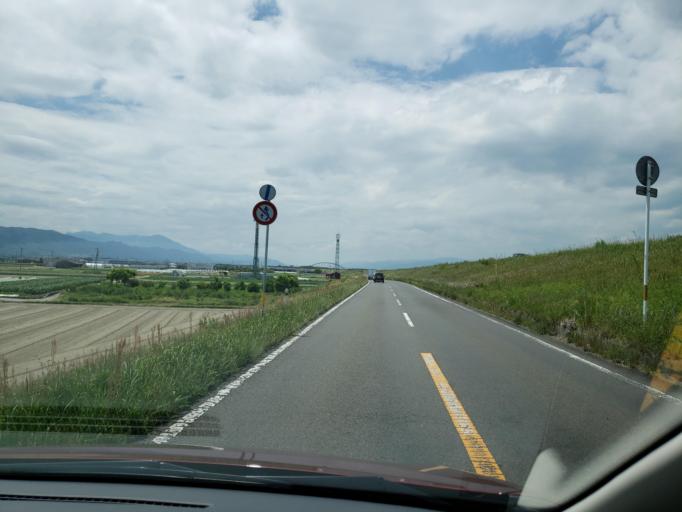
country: JP
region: Tokushima
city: Ishii
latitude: 34.0897
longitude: 134.4047
